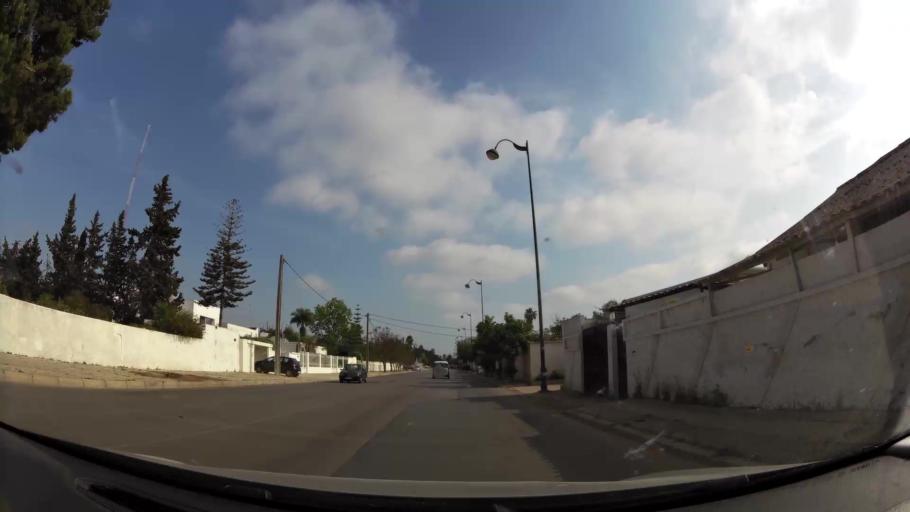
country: MA
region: Rabat-Sale-Zemmour-Zaer
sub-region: Rabat
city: Rabat
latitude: 33.9654
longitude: -6.8375
